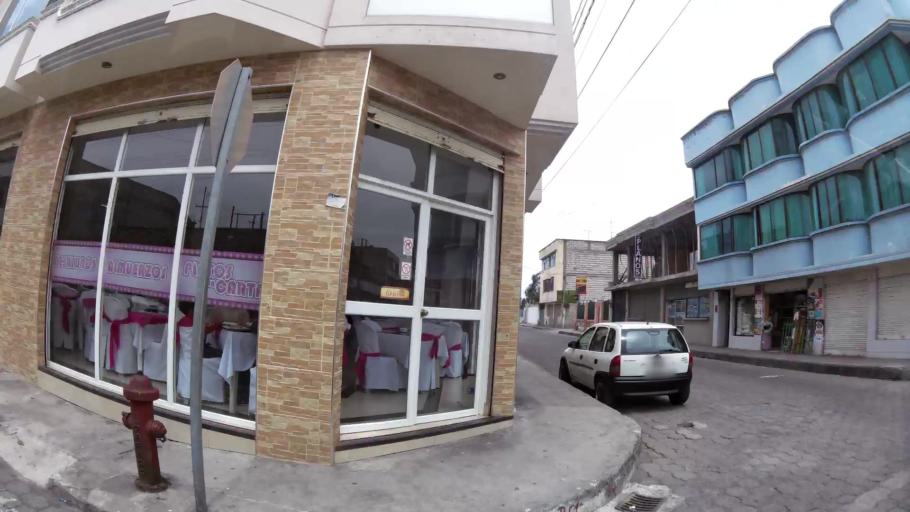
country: EC
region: Cotopaxi
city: San Miguel de Salcedo
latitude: -1.0416
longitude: -78.5899
